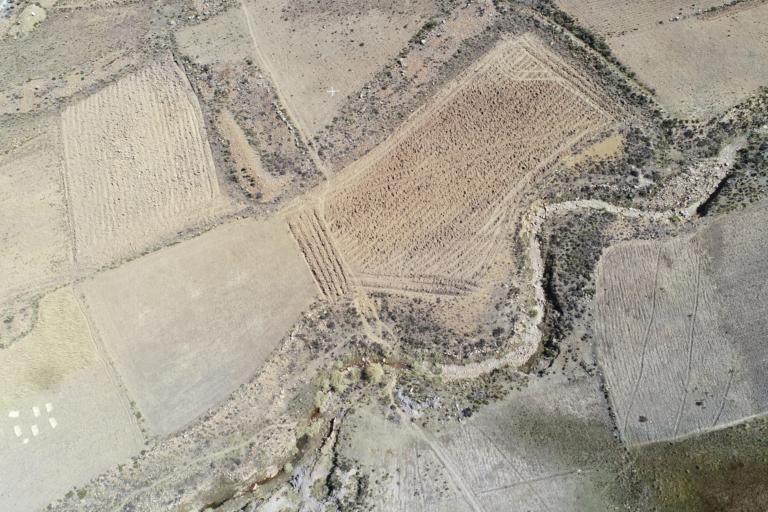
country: BO
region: La Paz
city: Achacachi
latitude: -15.8860
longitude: -68.8097
